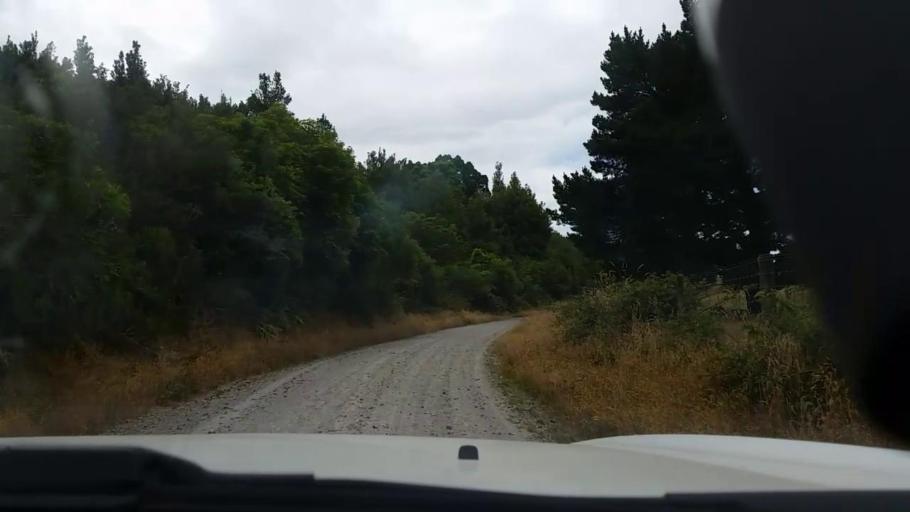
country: NZ
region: Bay of Plenty
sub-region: Rotorua District
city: Rotorua
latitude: -38.1582
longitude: 176.3699
